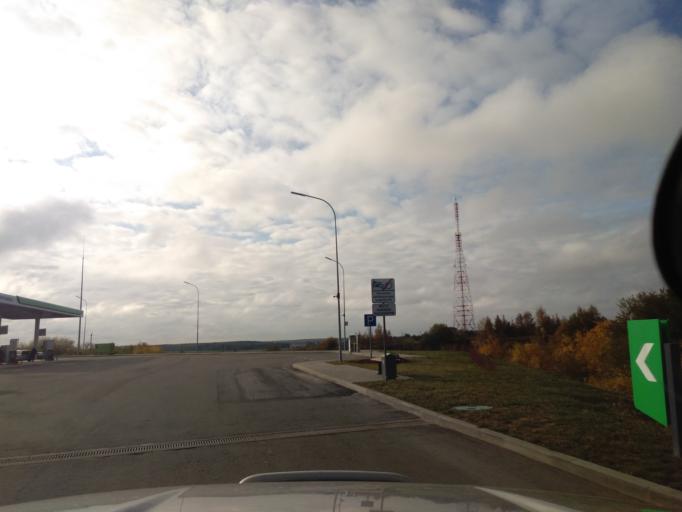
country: BY
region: Minsk
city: Kapyl'
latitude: 53.1494
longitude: 27.0733
